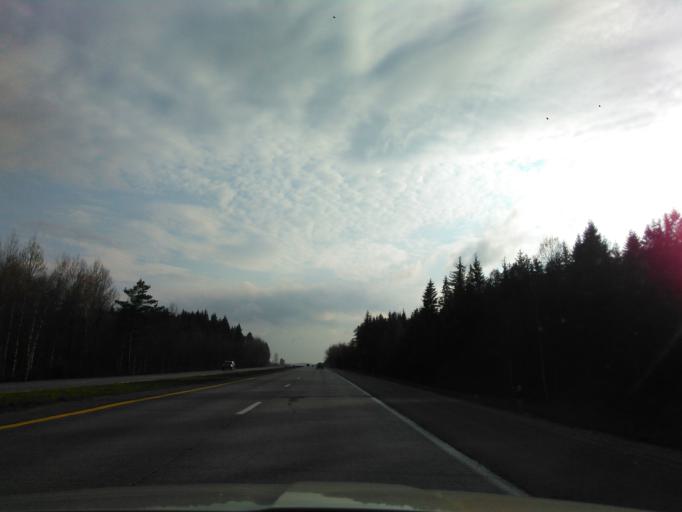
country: BY
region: Minsk
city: Astrashytski Haradok
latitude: 54.0894
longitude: 27.7652
